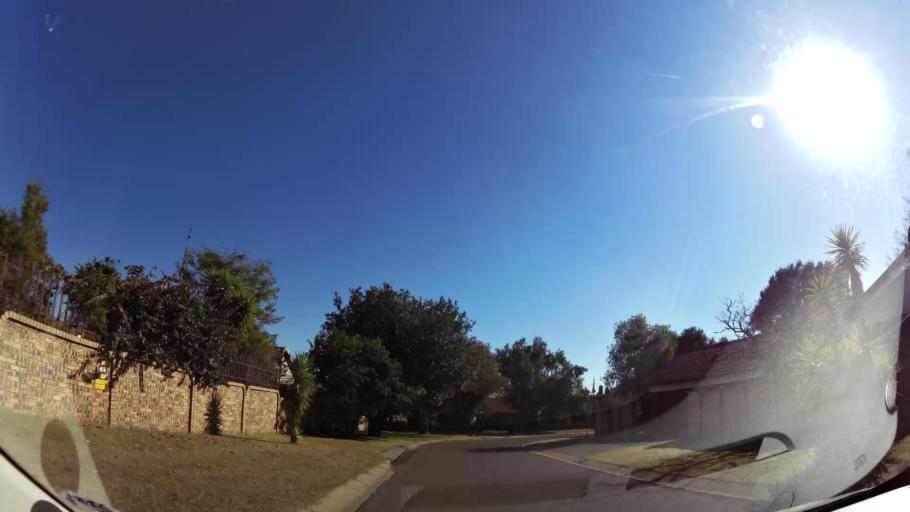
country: ZA
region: Mpumalanga
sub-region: Nkangala District Municipality
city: Witbank
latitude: -25.8874
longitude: 29.2531
